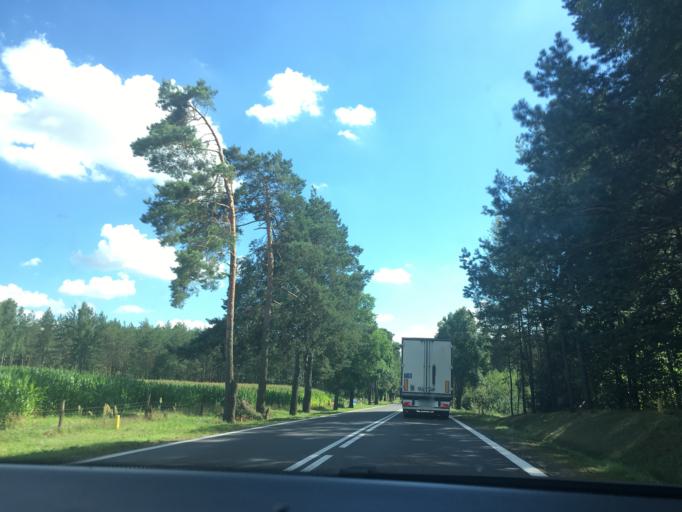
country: PL
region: Podlasie
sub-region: Powiat sokolski
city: Suchowola
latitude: 53.6436
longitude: 23.1197
